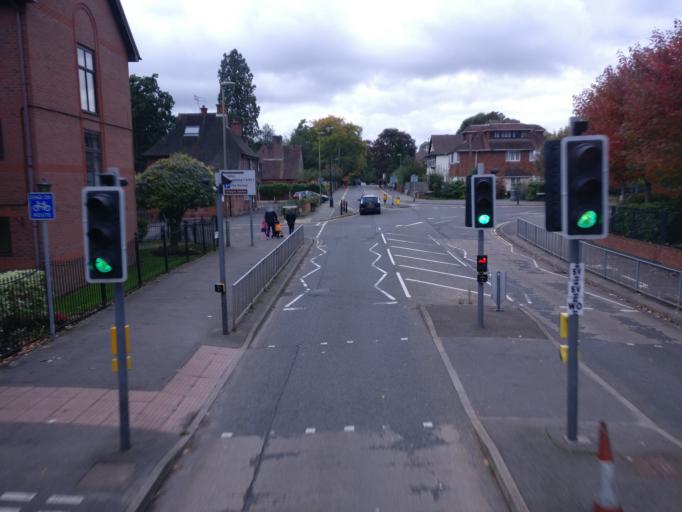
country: GB
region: England
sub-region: Surrey
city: Camberley
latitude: 51.3360
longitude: -0.7484
